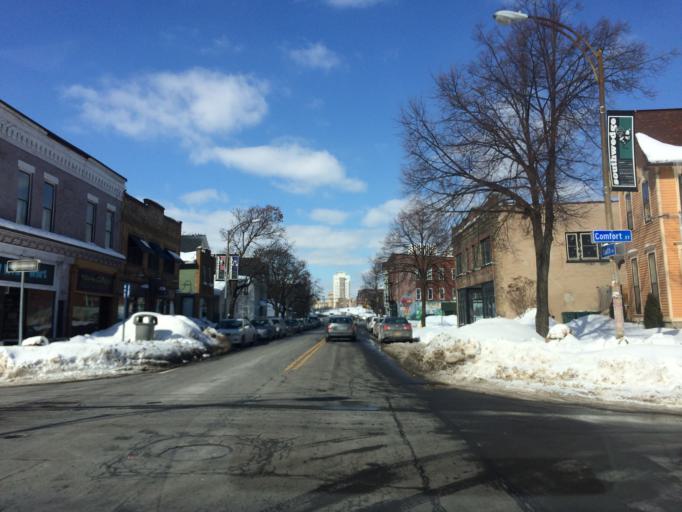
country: US
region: New York
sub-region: Monroe County
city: Rochester
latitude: 43.1471
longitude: -77.6057
